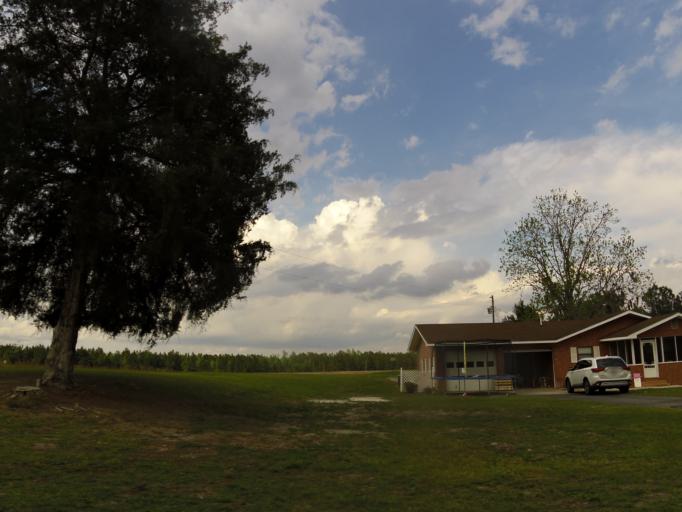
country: US
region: Georgia
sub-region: Charlton County
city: Folkston
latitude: 30.8093
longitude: -82.0632
